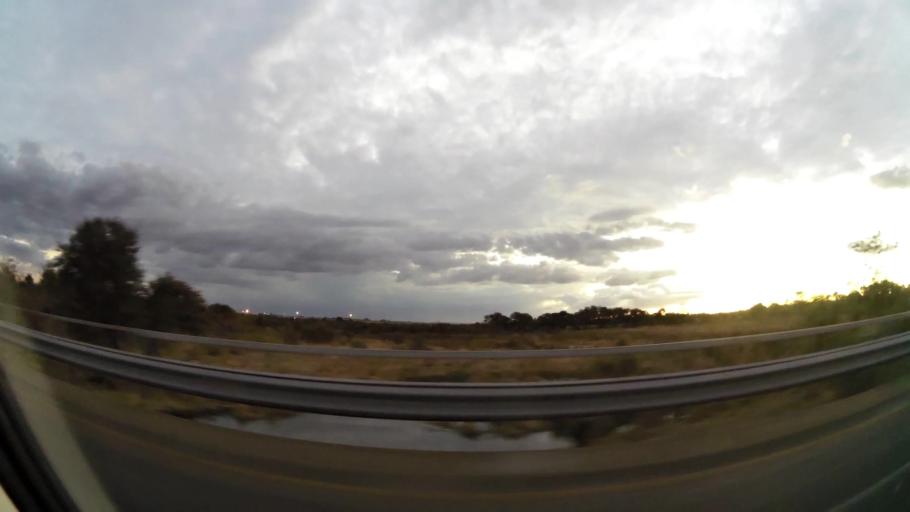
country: ZA
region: Limpopo
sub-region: Capricorn District Municipality
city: Polokwane
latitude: -23.8246
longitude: 29.4258
